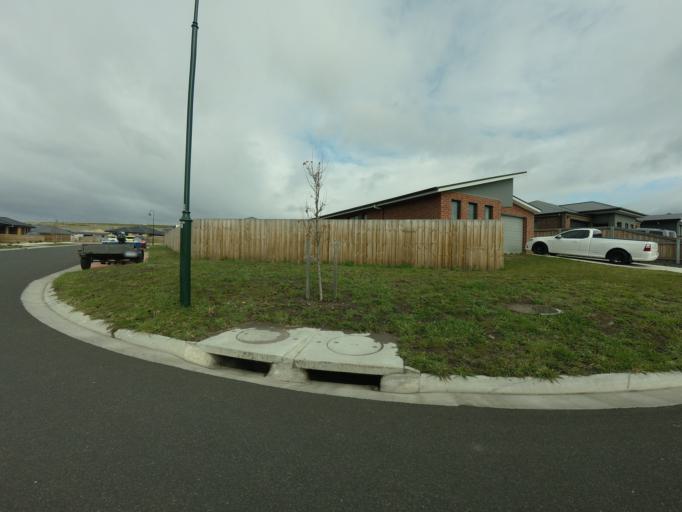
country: AU
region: Tasmania
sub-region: Clarence
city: Rokeby
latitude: -42.8842
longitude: 147.4307
